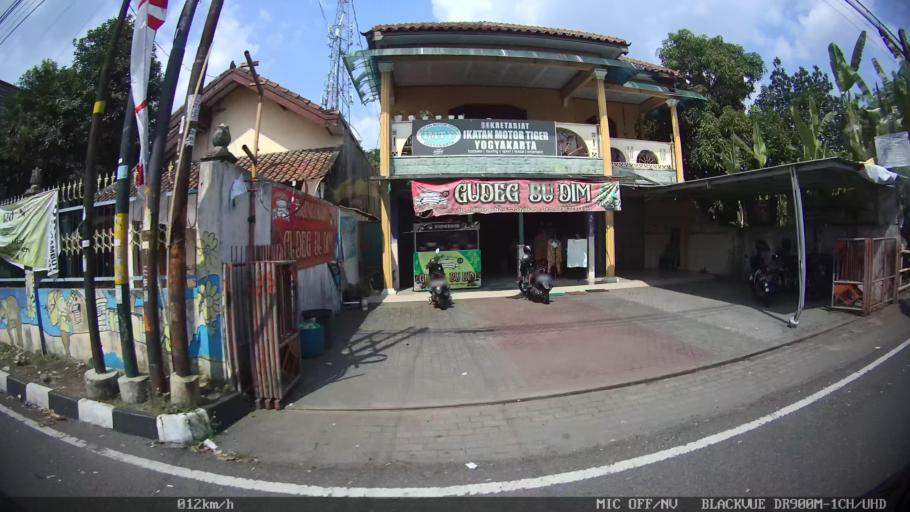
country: ID
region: Daerah Istimewa Yogyakarta
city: Yogyakarta
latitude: -7.8184
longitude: 110.3908
